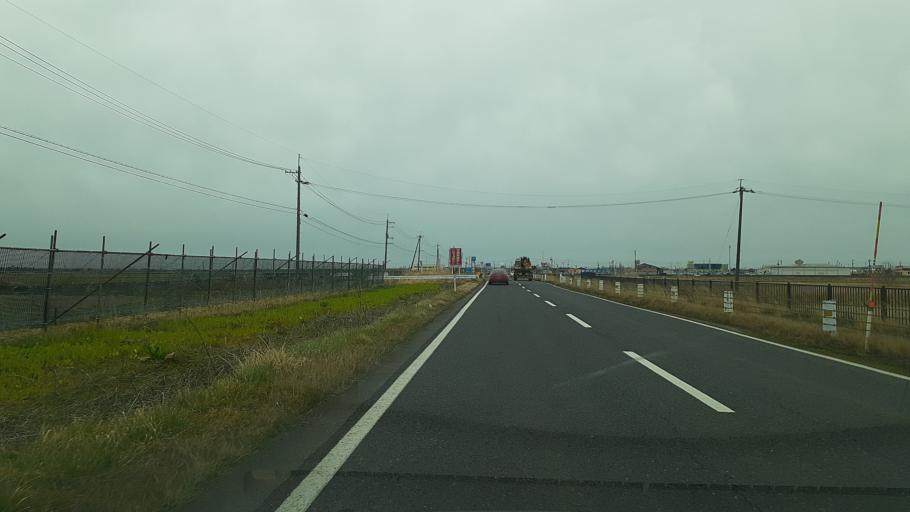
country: JP
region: Niigata
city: Niitsu-honcho
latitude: 37.8098
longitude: 139.1010
